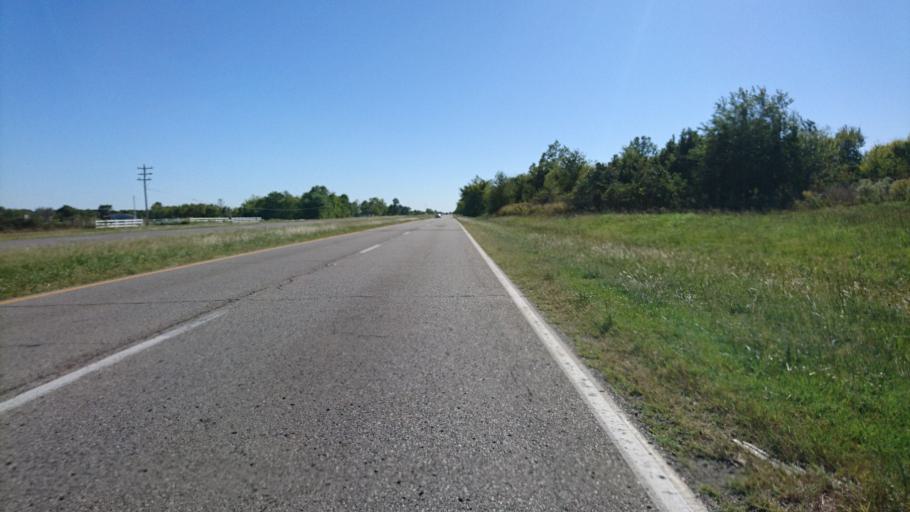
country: US
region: Oklahoma
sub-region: Rogers County
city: Bushyhead
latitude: 36.4061
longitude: -95.5419
